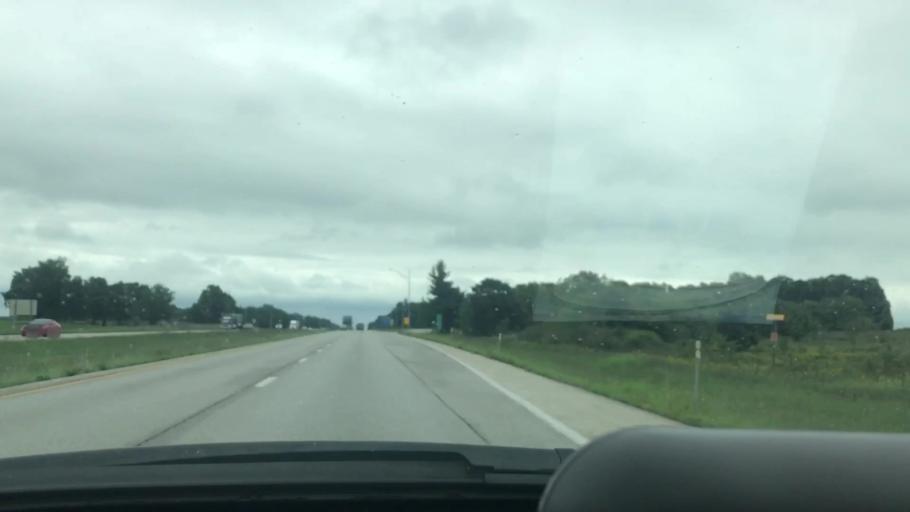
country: US
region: Missouri
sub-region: Lawrence County
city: Mount Vernon
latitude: 37.1368
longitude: -93.7264
